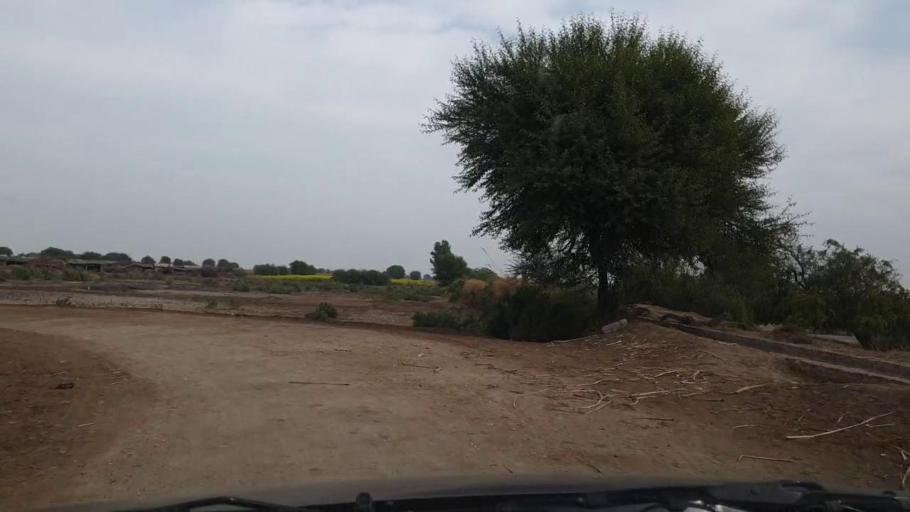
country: PK
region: Sindh
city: Sanghar
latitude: 26.0942
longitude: 68.8814
